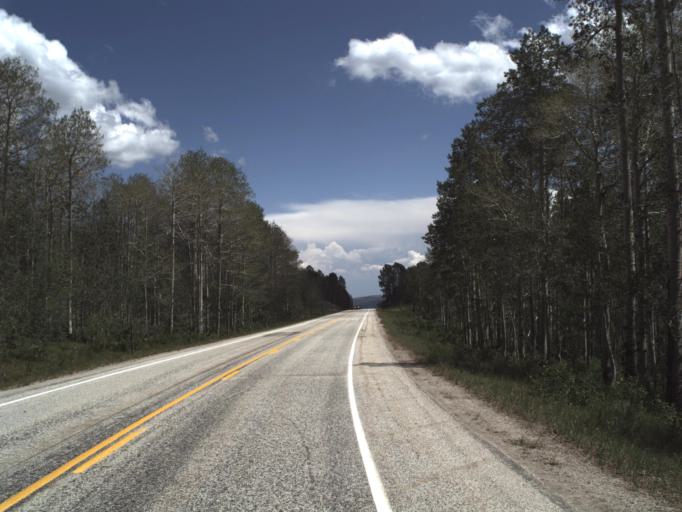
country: US
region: Utah
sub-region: Rich County
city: Randolph
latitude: 41.4748
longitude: -111.4869
